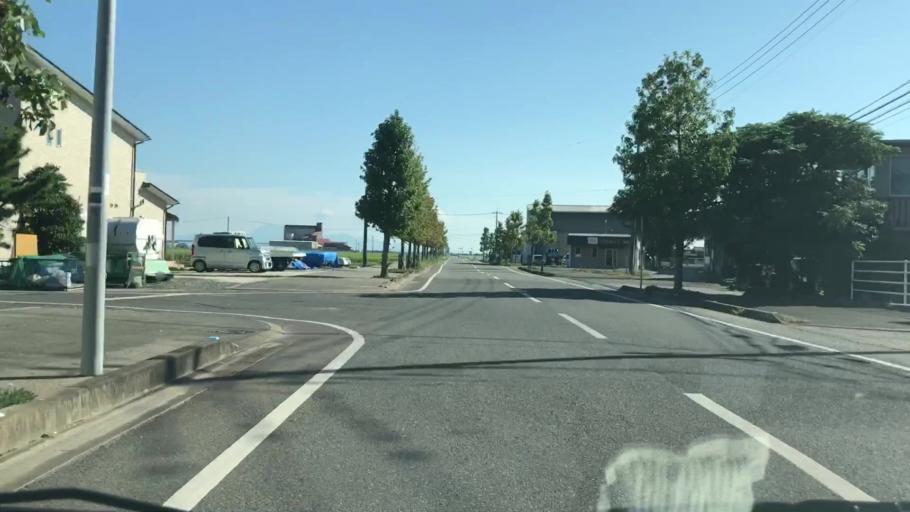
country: JP
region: Saga Prefecture
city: Okawa
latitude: 33.1806
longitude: 130.3132
